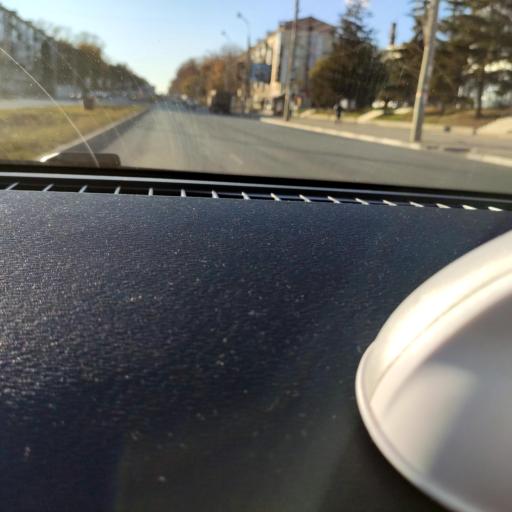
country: RU
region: Samara
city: Samara
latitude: 53.2010
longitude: 50.1998
